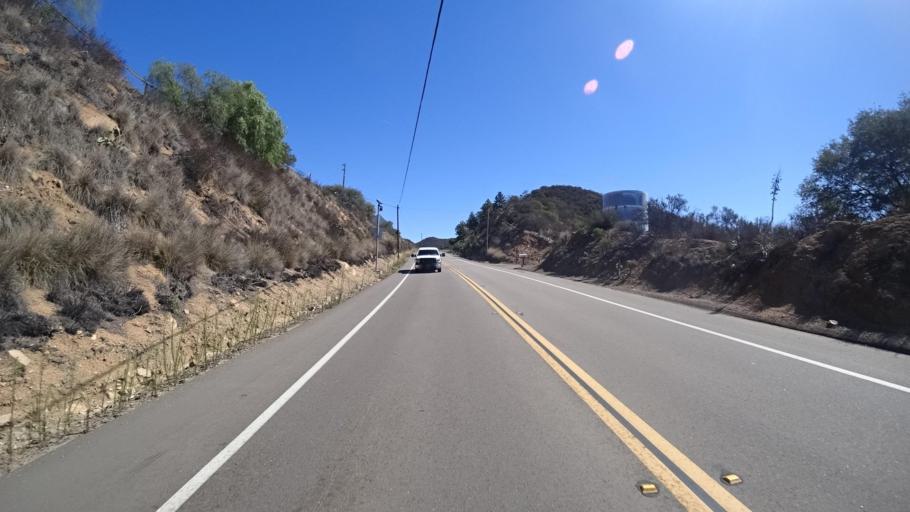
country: US
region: California
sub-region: San Diego County
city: Jamul
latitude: 32.7329
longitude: -116.8189
